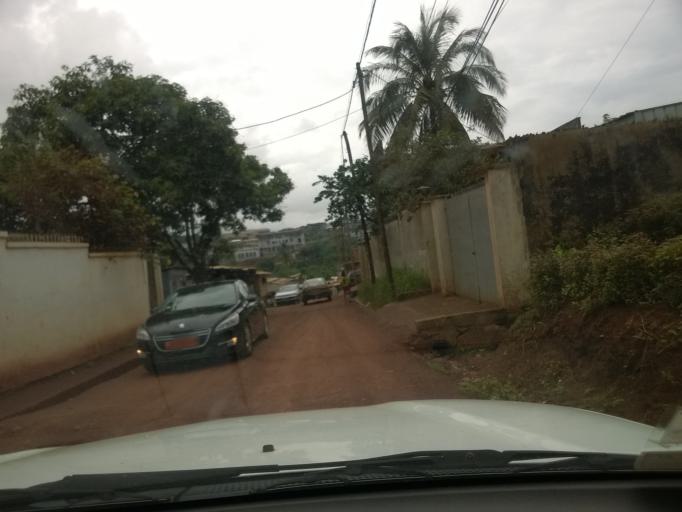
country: CM
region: Centre
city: Yaounde
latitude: 3.9051
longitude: 11.5265
